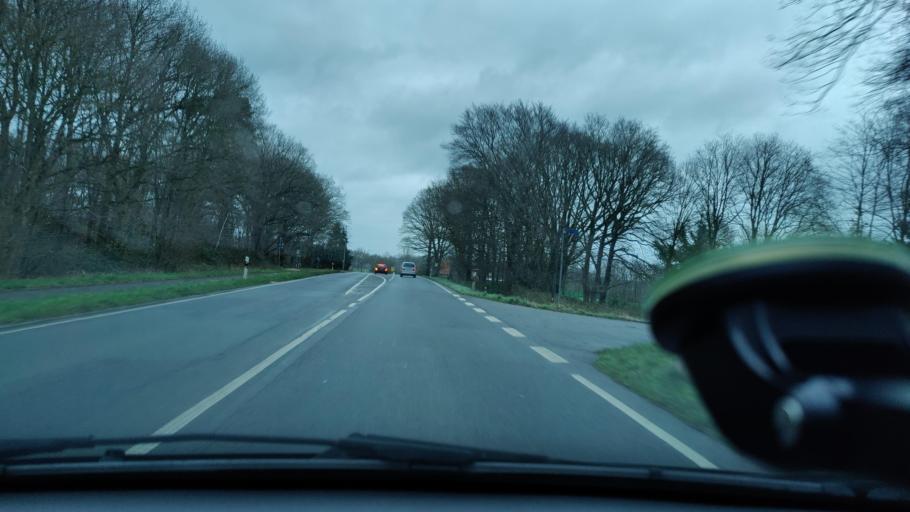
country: DE
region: North Rhine-Westphalia
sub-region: Regierungsbezirk Dusseldorf
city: Weeze
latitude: 51.6102
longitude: 6.1734
